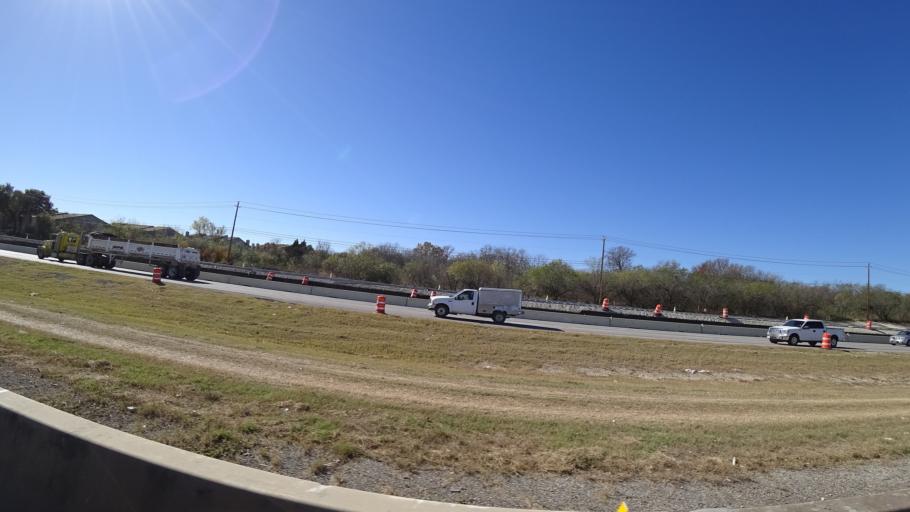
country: US
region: Texas
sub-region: Travis County
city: Austin
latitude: 30.3074
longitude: -97.6610
